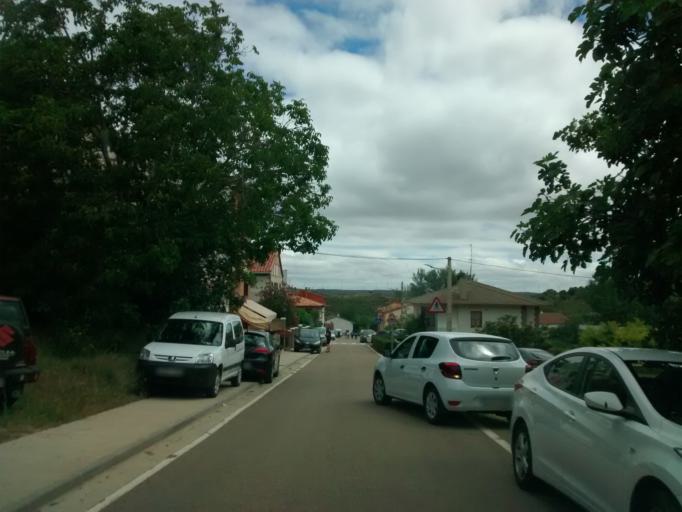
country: ES
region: Aragon
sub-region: Provincia de Zaragoza
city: Lituenigo
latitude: 41.8341
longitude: -1.7619
